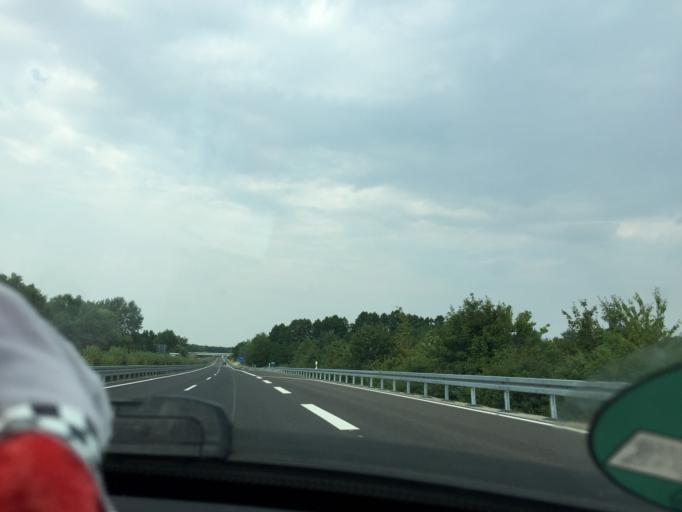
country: DE
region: Brandenburg
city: Schipkau
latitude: 51.5391
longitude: 13.9099
